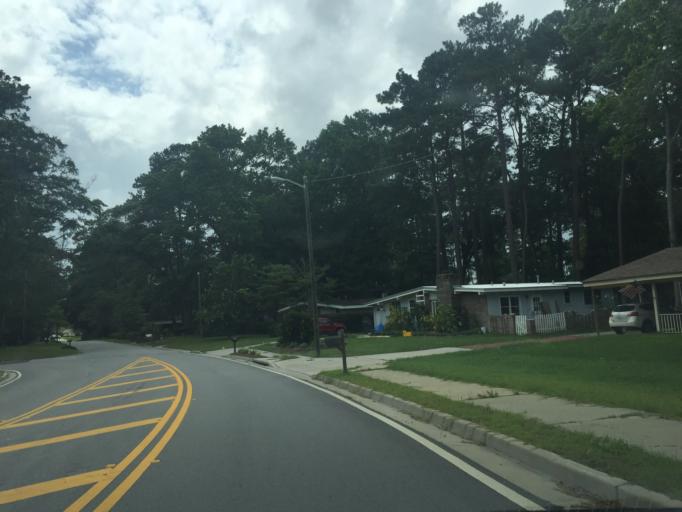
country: US
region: Georgia
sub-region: Chatham County
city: Montgomery
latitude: 31.9812
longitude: -81.1060
